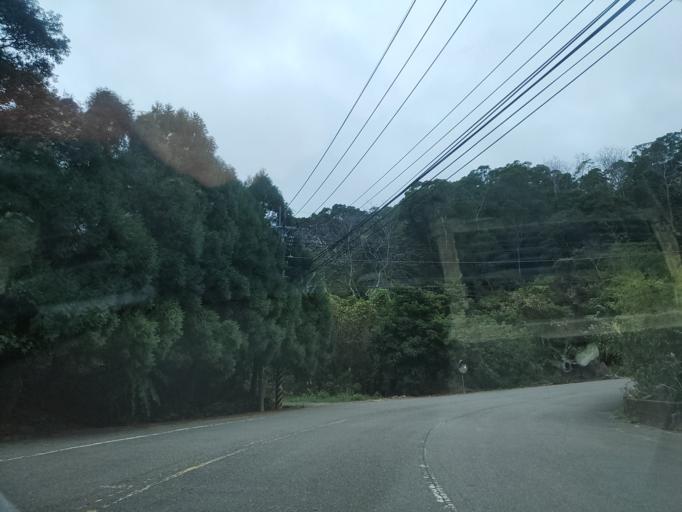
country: TW
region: Taiwan
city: Fengyuan
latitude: 24.3676
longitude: 120.7756
